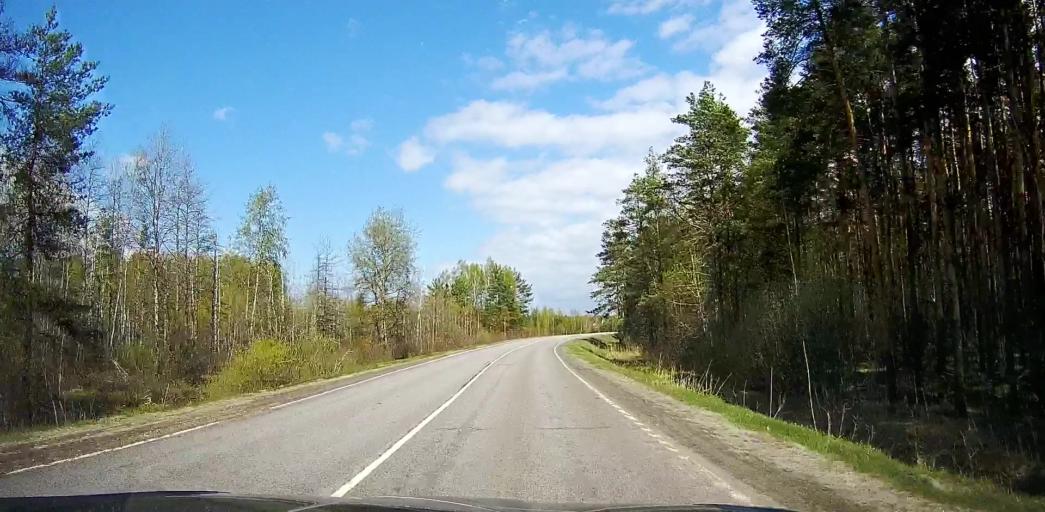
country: RU
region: Moskovskaya
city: Davydovo
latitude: 55.5512
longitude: 38.8184
